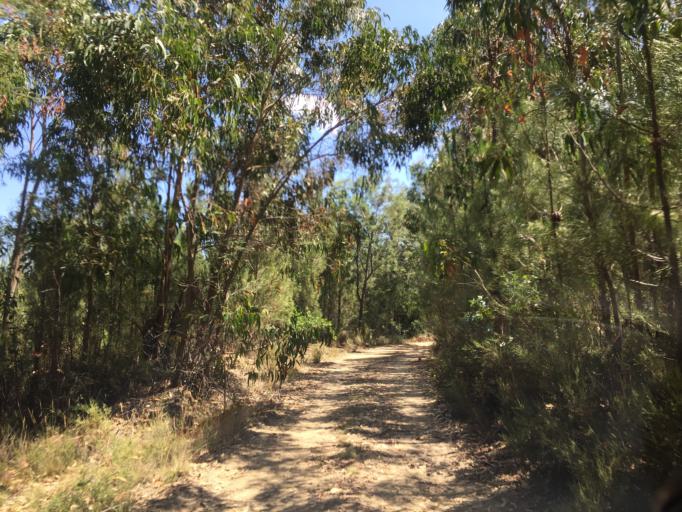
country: PT
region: Coimbra
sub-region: Pampilhosa da Serra
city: Pampilhosa da Serra
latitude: 40.1014
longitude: -7.8456
